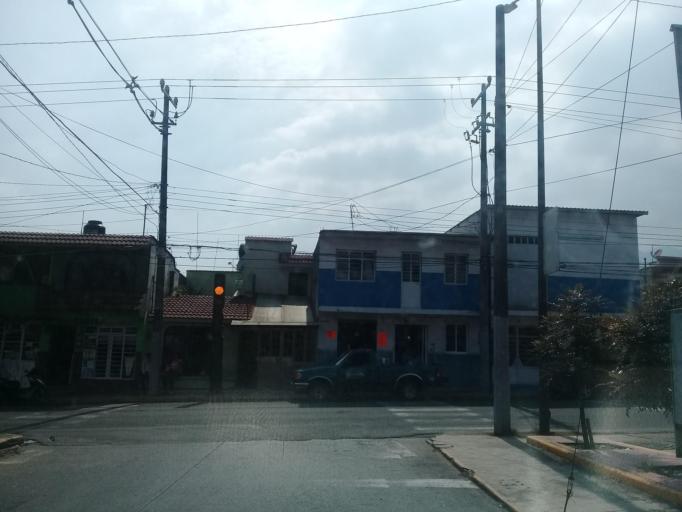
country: MX
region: Veracruz
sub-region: Mariano Escobedo
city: Palmira
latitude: 18.8755
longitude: -97.1057
